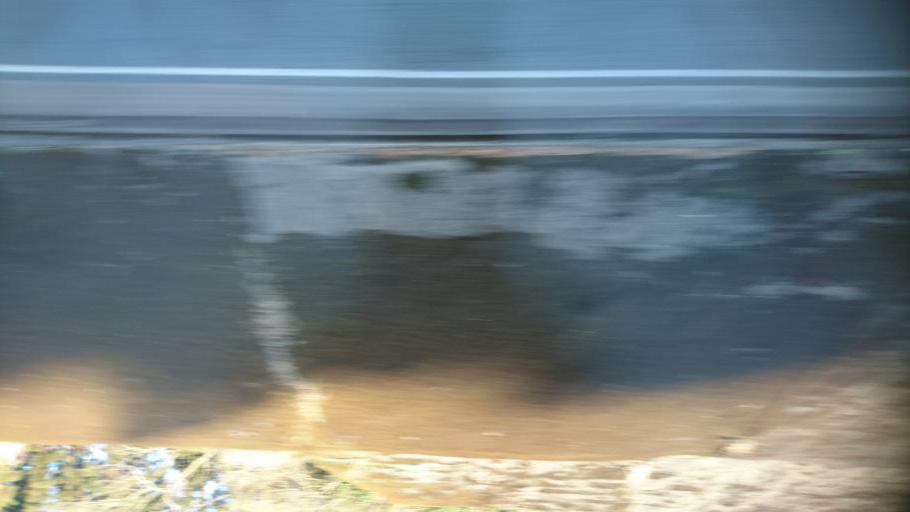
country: JP
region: Miyazaki
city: Miyakonojo
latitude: 31.7952
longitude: 131.1730
